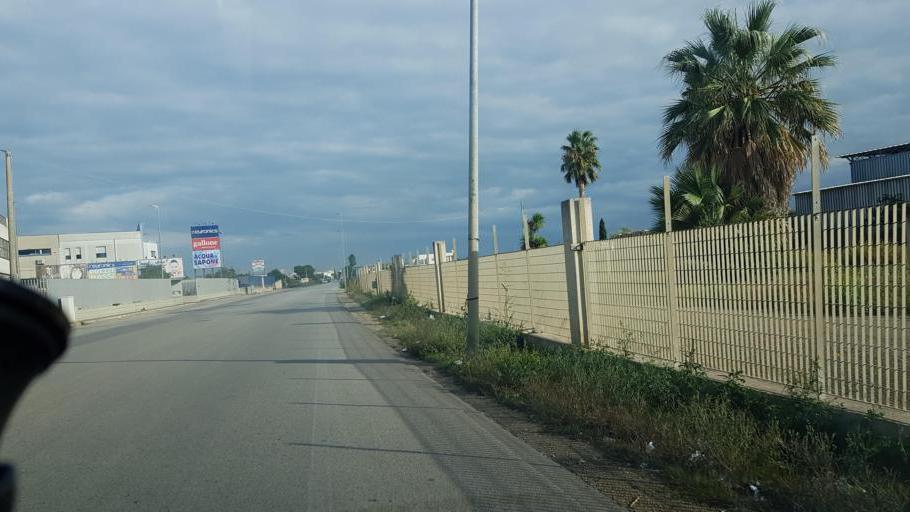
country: IT
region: Apulia
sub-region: Provincia di Brindisi
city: Francavilla Fontana
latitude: 40.5322
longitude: 17.5613
